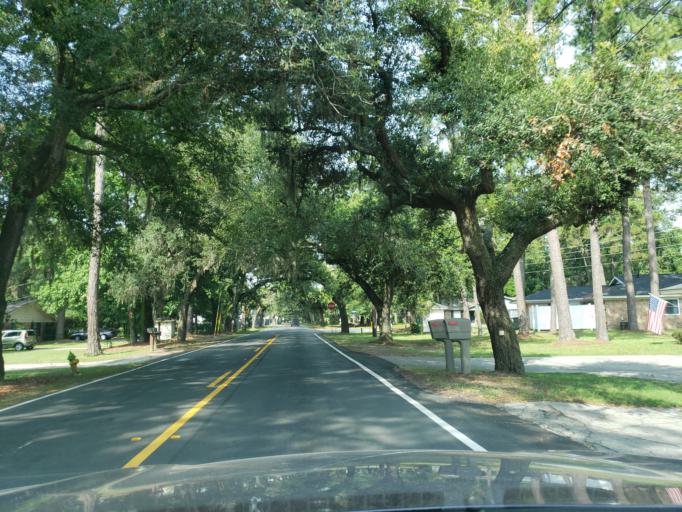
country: US
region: Georgia
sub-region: Chatham County
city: Wilmington Island
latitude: 32.0228
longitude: -80.9686
